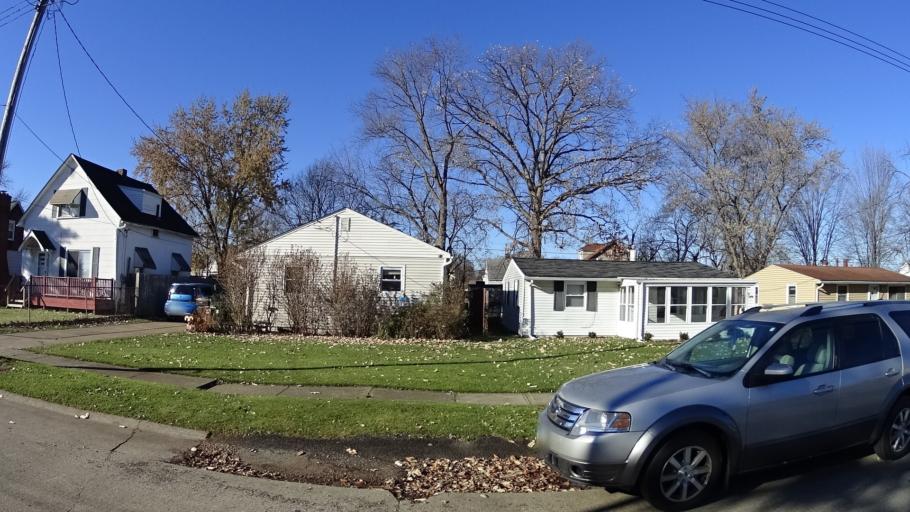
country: US
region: Ohio
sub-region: Lorain County
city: Elyria
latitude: 41.3804
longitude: -82.0764
